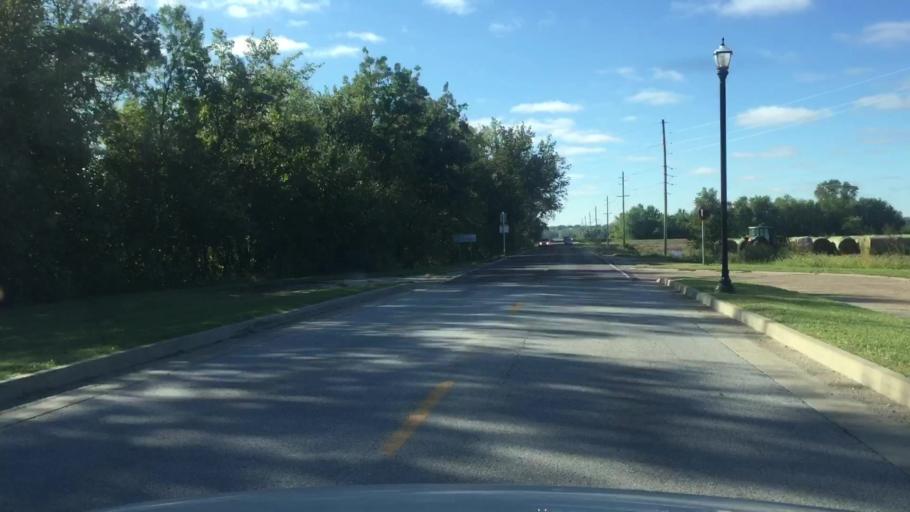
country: US
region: Missouri
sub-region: Howard County
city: New Franklin
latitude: 39.0103
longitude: -92.7379
